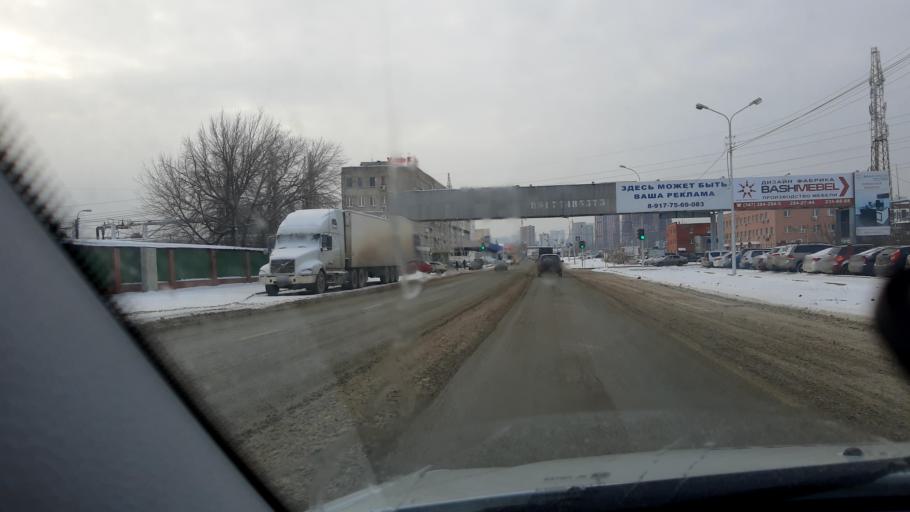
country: RU
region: Bashkortostan
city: Ufa
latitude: 54.7939
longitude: 56.0636
